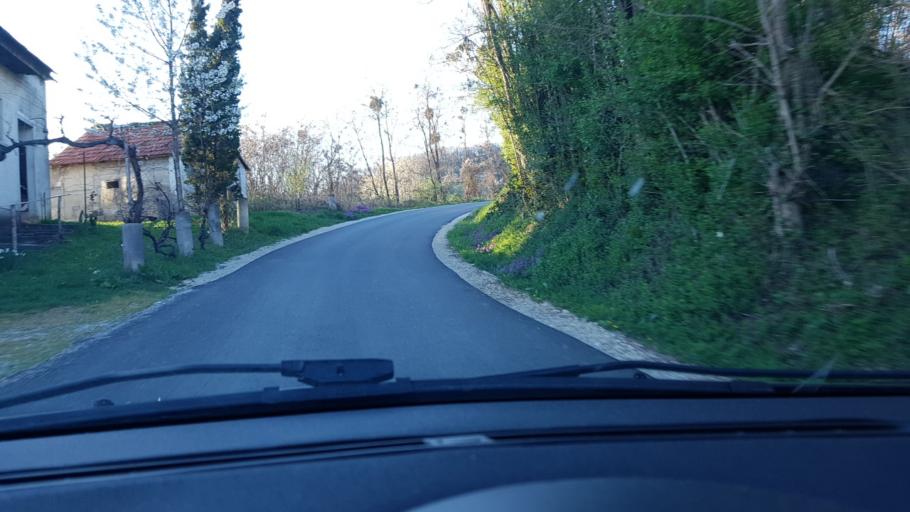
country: HR
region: Krapinsko-Zagorska
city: Pregrada
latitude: 46.1602
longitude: 15.7095
